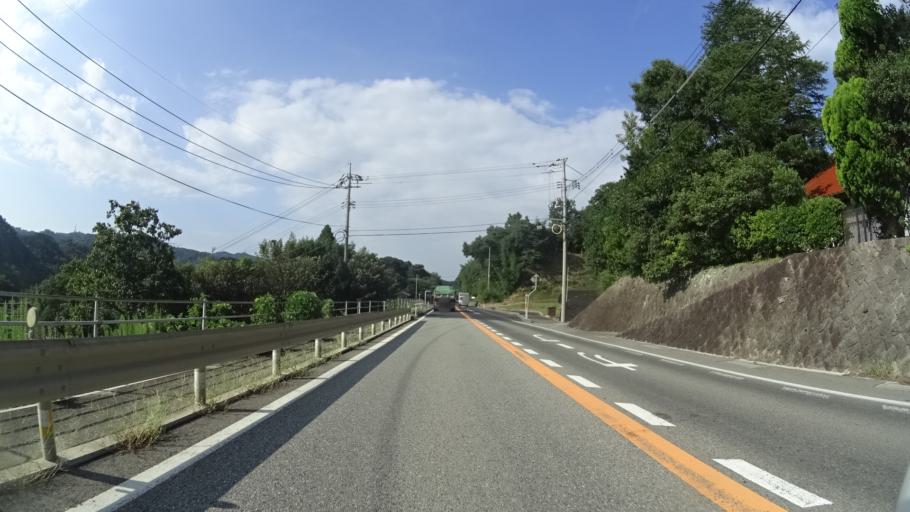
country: JP
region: Shimane
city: Odacho-oda
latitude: 35.2492
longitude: 132.5600
